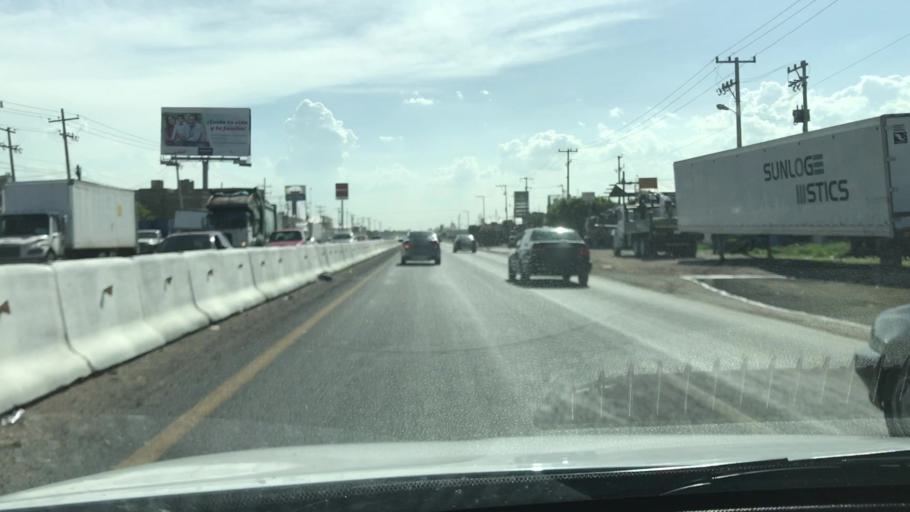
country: MX
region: Guanajuato
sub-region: Celaya
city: Colonia Pedro Maria Anaya
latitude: 20.5179
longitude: -100.8597
